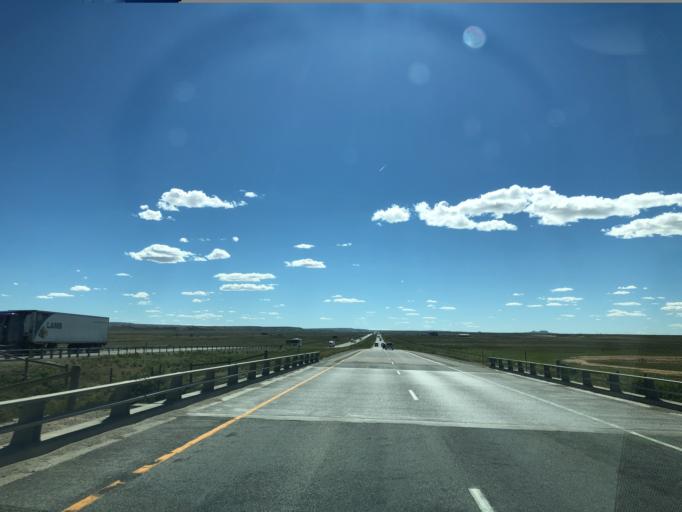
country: US
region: Wyoming
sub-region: Carbon County
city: Rawlins
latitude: 41.6700
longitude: -107.9987
